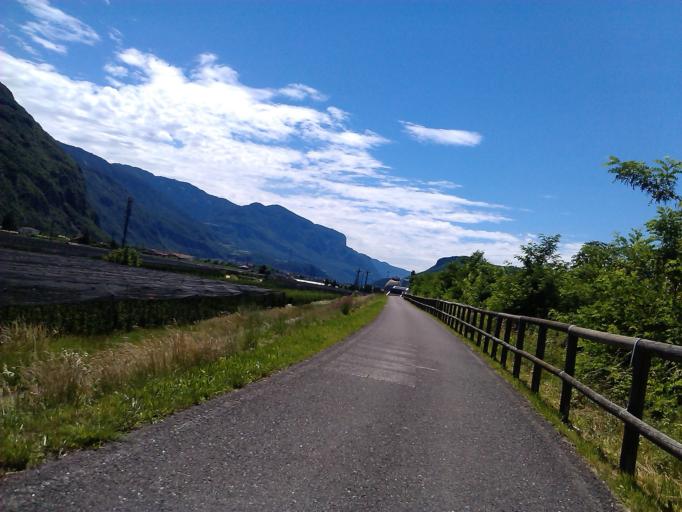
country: IT
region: Trentino-Alto Adige
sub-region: Bolzano
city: Vadena
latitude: 46.4120
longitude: 11.3147
